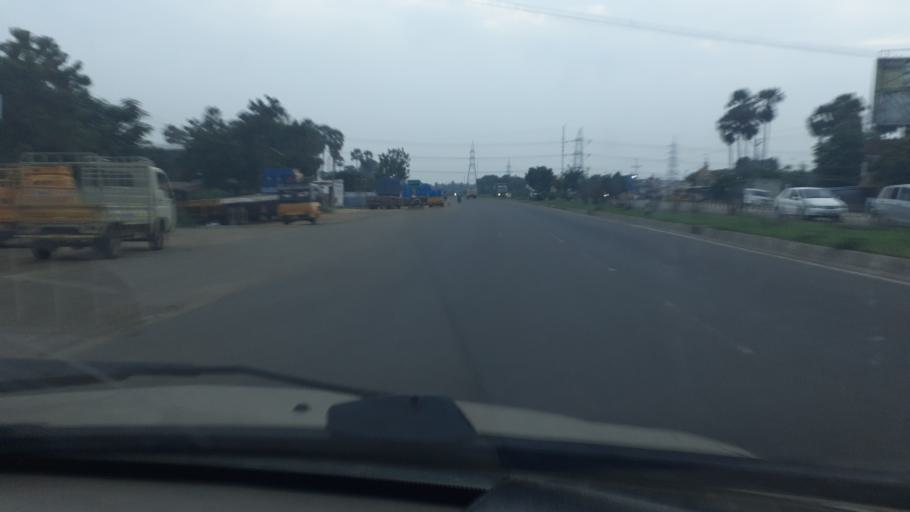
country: IN
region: Tamil Nadu
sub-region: Thoothukkudi
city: Korampallam
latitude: 8.7746
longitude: 78.0869
